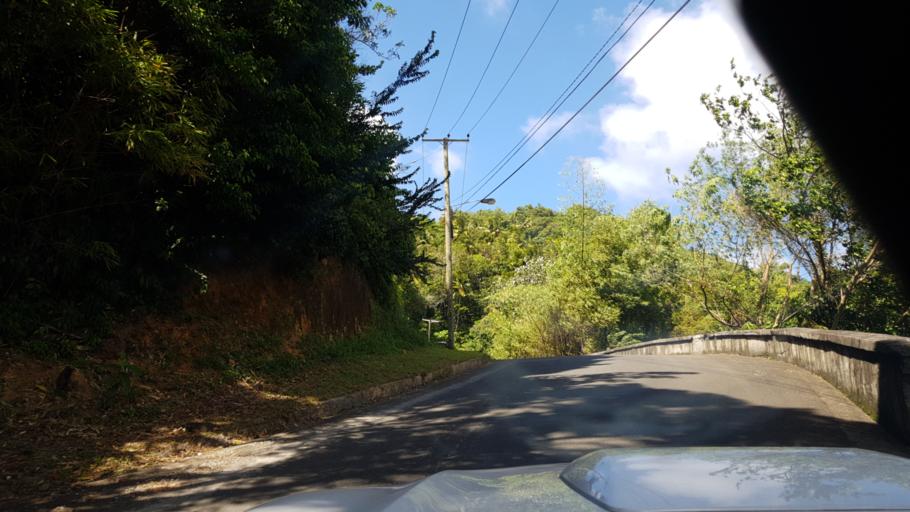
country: LC
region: Castries Quarter
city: Castries
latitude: 13.9820
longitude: -60.9736
